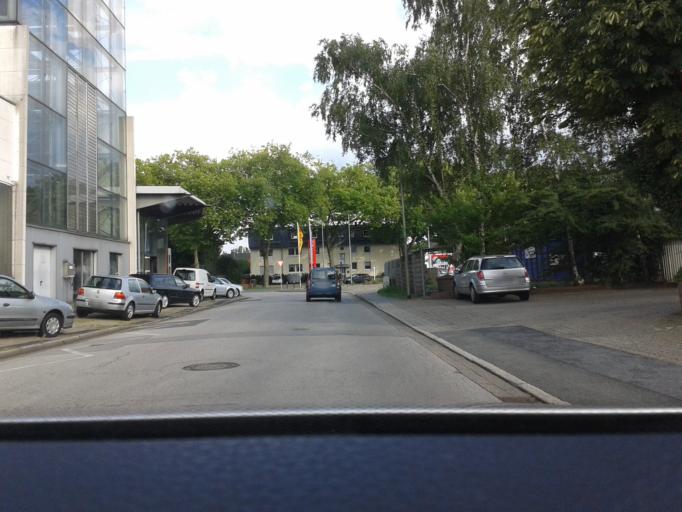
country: DE
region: North Rhine-Westphalia
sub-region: Regierungsbezirk Dusseldorf
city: Hochfeld
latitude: 51.4171
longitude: 6.6963
